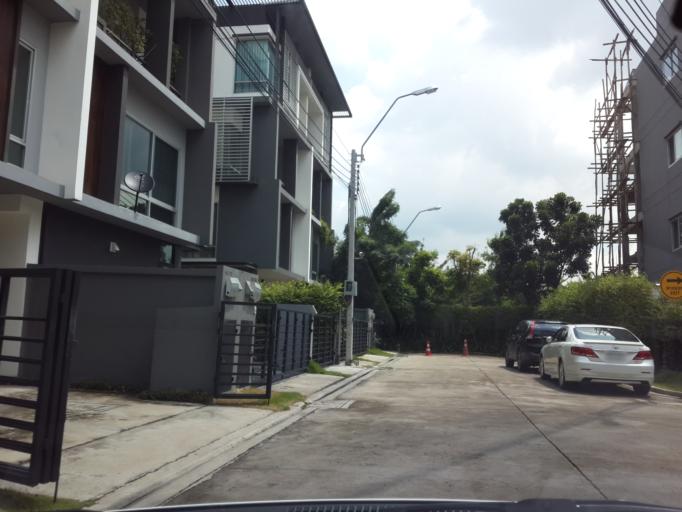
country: TH
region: Bangkok
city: Wang Thonglang
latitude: 13.7721
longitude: 100.5998
